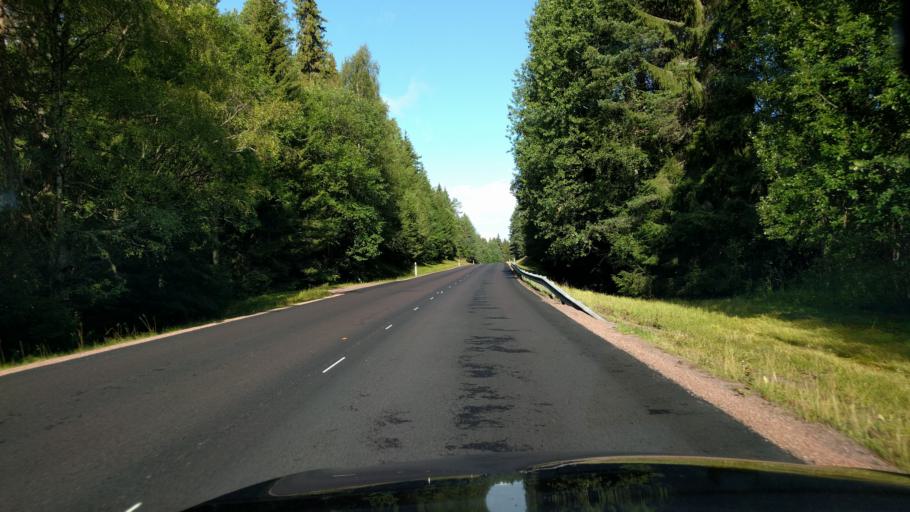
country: SE
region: Dalarna
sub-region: Mora Kommun
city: Mora
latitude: 61.0872
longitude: 14.3159
